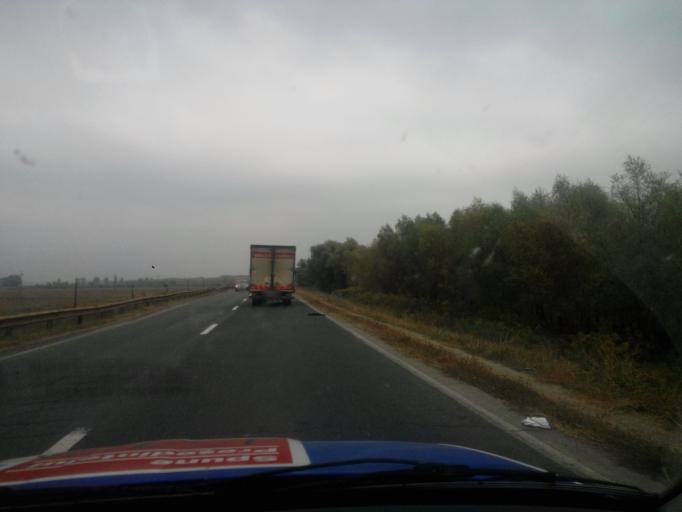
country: RO
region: Braila
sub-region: Municipiul Braila
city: Braila
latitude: 45.3175
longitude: 27.9882
